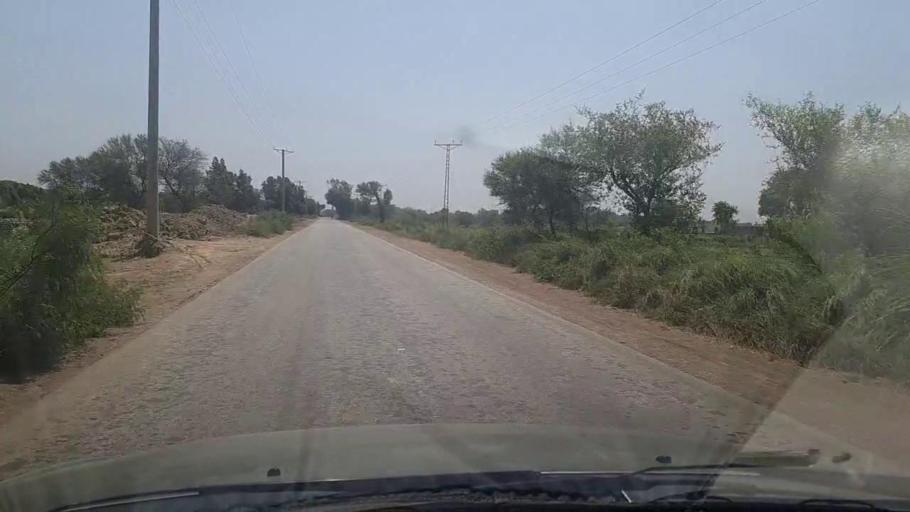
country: PK
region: Sindh
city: Hyderabad
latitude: 25.3804
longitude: 68.4509
